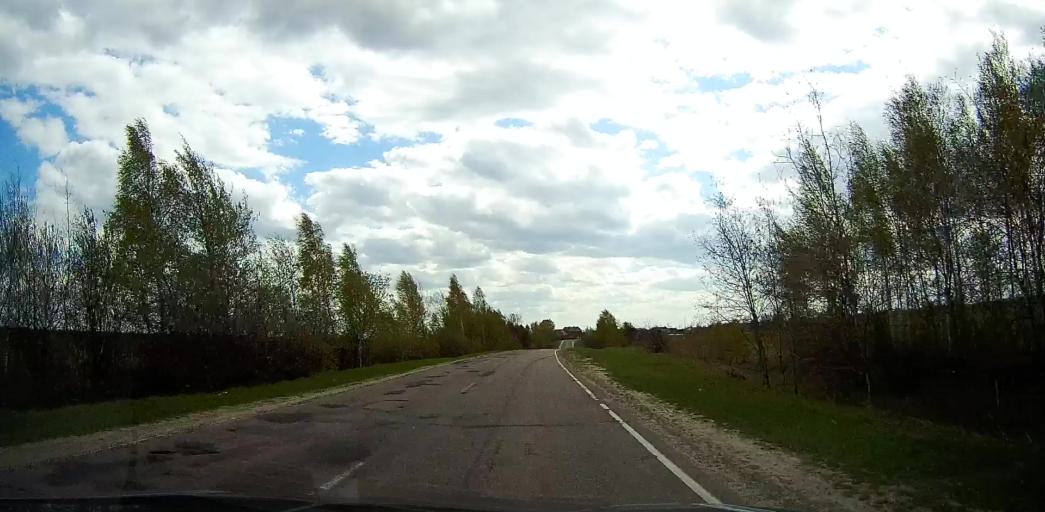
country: RU
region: Moskovskaya
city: Davydovo
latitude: 55.6351
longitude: 38.7466
